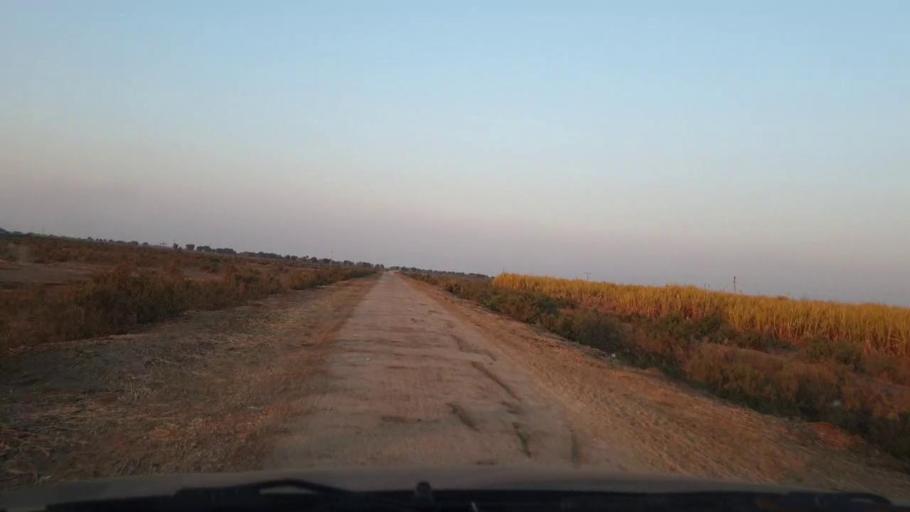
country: PK
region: Sindh
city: Jhol
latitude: 25.9270
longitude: 68.9659
